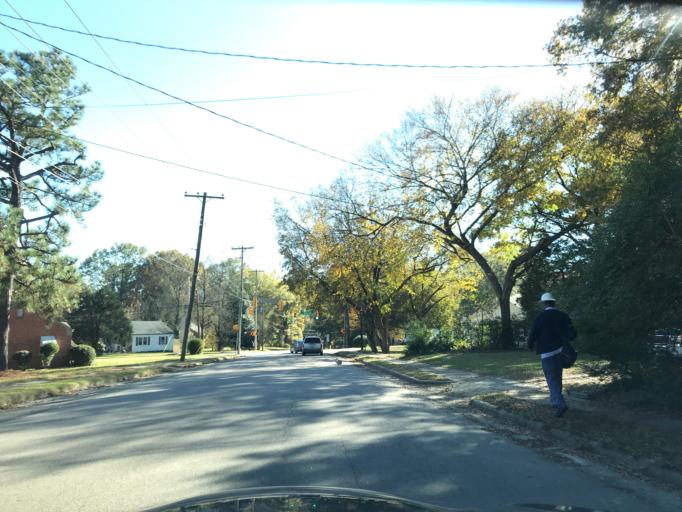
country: US
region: North Carolina
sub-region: Wake County
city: Raleigh
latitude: 35.7896
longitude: -78.6096
